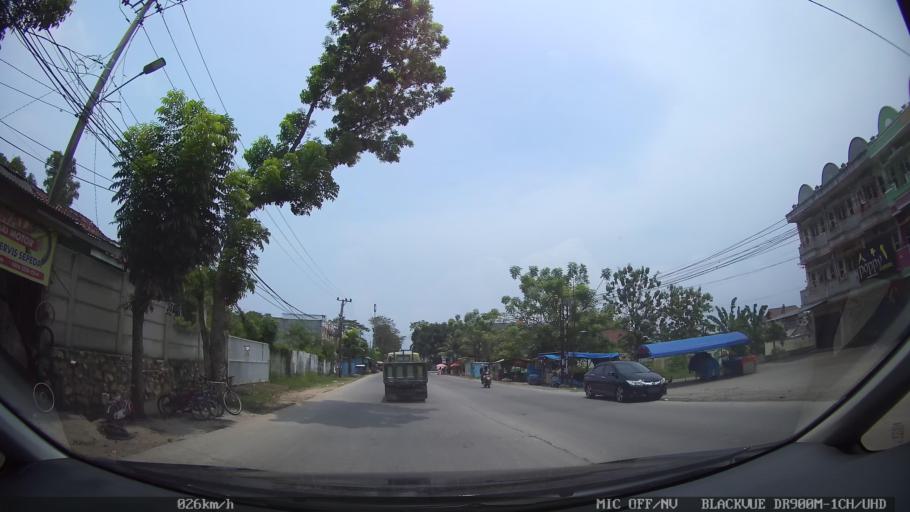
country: ID
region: Lampung
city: Kedaton
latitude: -5.3947
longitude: 105.2931
